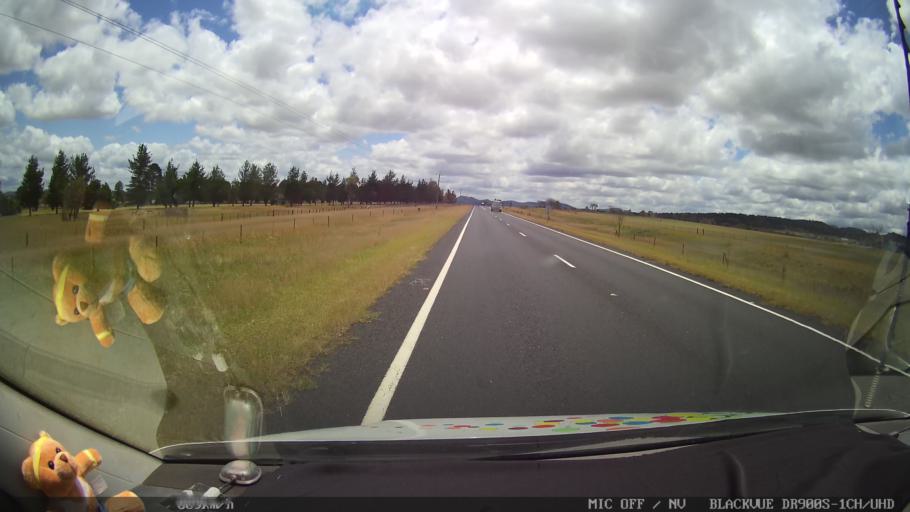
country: AU
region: New South Wales
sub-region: Glen Innes Severn
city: Glen Innes
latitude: -29.4314
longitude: 151.8547
